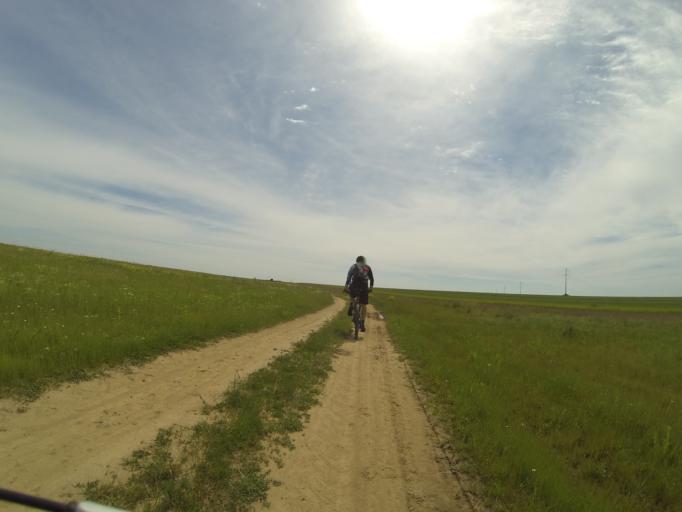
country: RO
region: Dolj
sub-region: Comuna Ghindeni
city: Ghindeni
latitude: 44.2070
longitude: 23.9495
